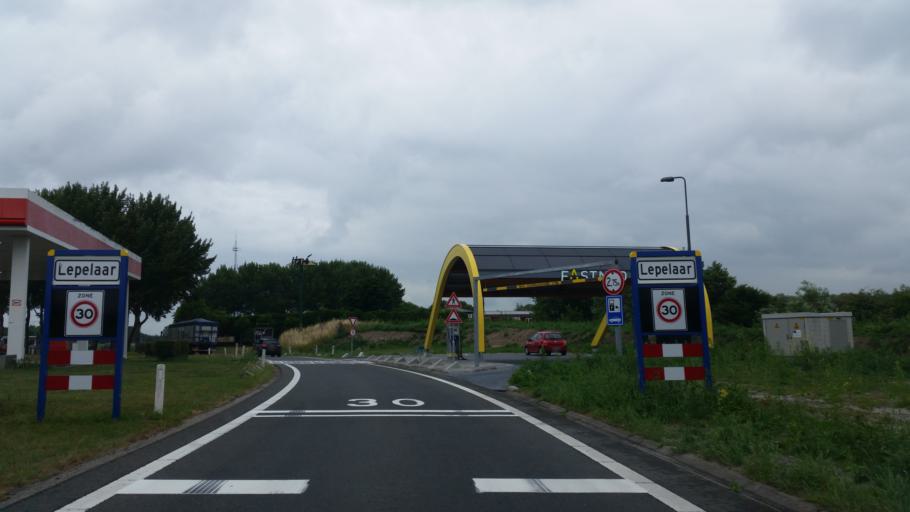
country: NL
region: Flevoland
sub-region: Gemeente Lelystad
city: Lelystad
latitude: 52.4326
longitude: 5.4224
